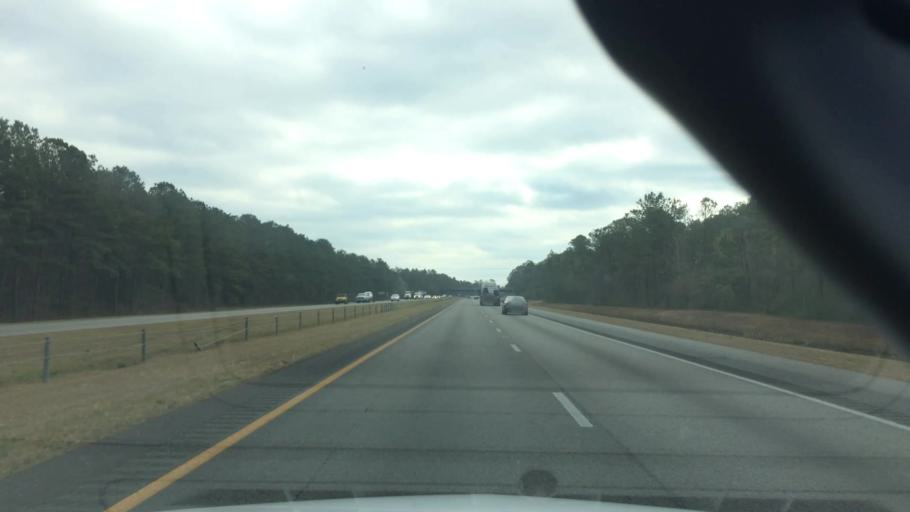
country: US
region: North Carolina
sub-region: New Hanover County
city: Skippers Corner
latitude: 34.3334
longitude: -77.8759
